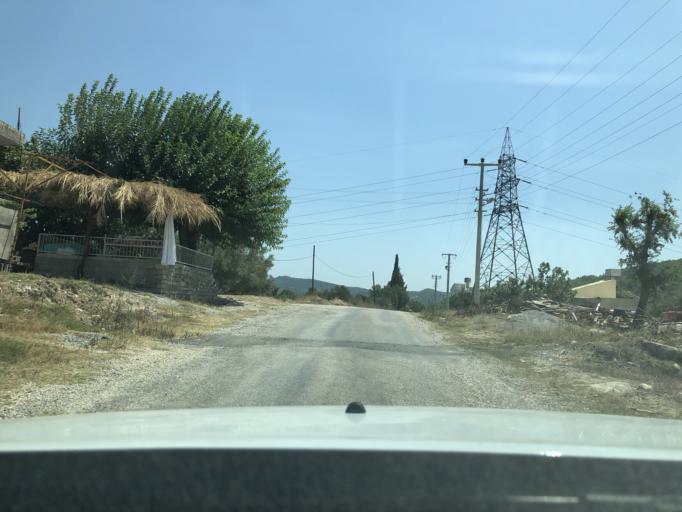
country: TR
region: Antalya
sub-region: Manavgat
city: Kizilagac
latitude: 36.8576
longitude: 31.5566
